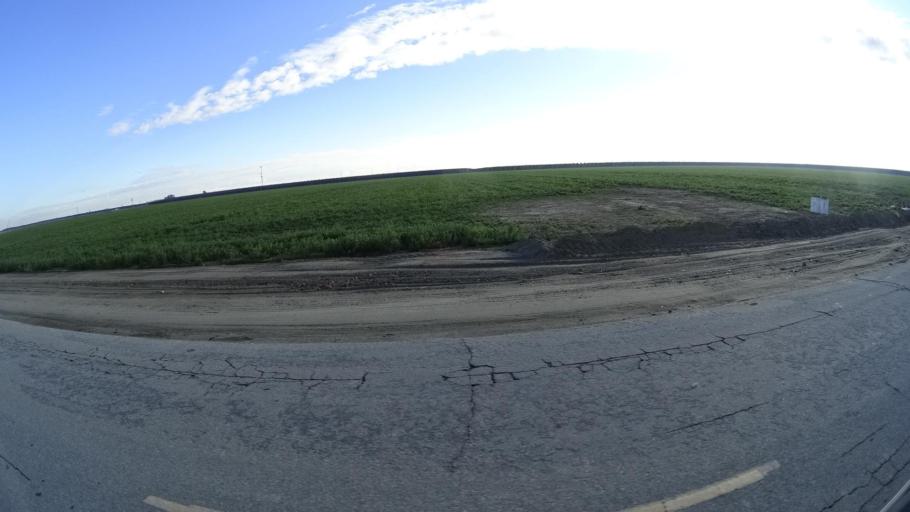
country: US
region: California
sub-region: Kern County
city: Delano
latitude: 35.7472
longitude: -119.3300
